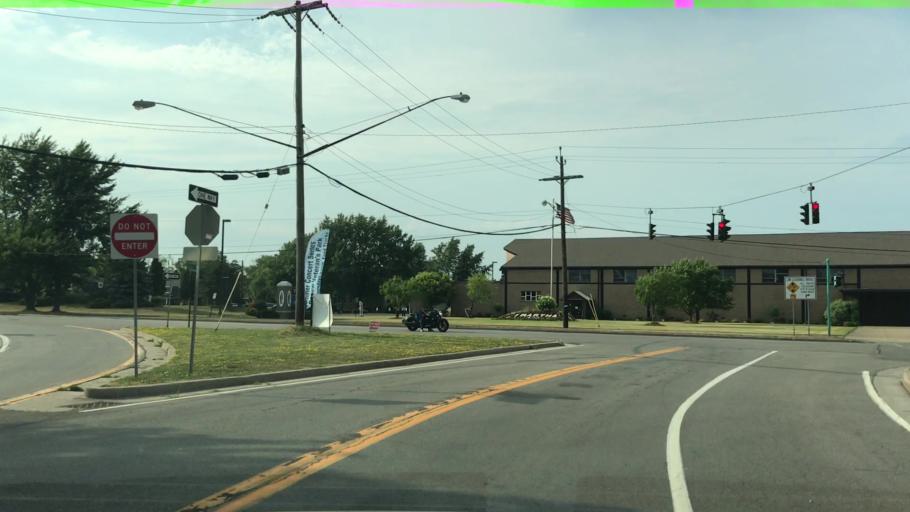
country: US
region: New York
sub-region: Erie County
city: Depew
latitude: 42.9183
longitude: -78.7137
